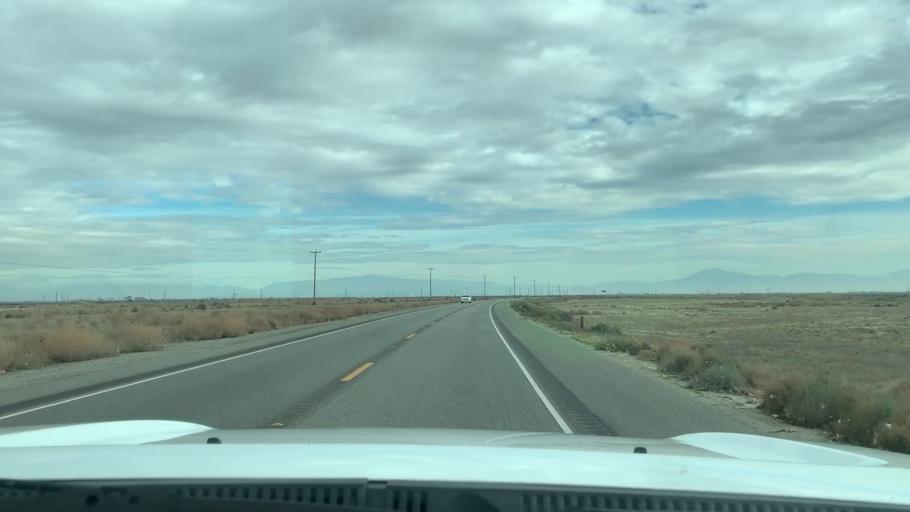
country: US
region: California
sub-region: Kern County
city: Ford City
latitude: 35.2673
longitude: -119.3053
